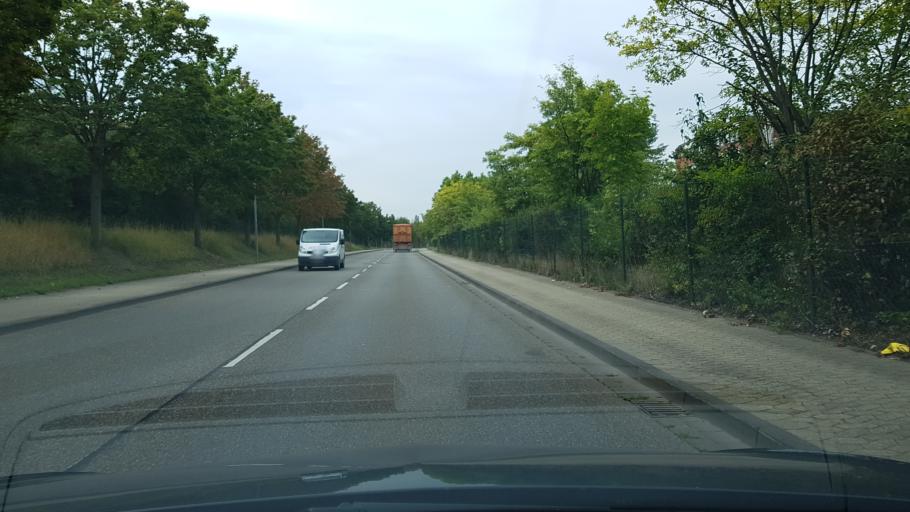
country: DE
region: Rheinland-Pfalz
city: Niederwerth
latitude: 50.3810
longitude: 7.5997
